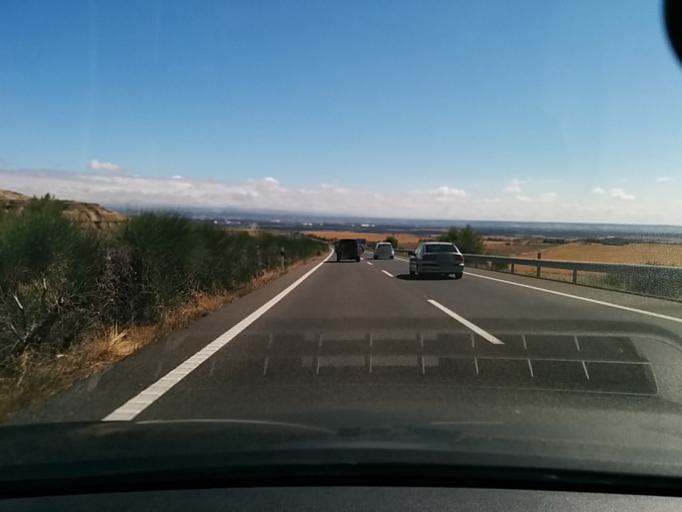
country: ES
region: Aragon
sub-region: Provincia de Huesca
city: Almudebar
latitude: 42.0738
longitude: -0.5013
